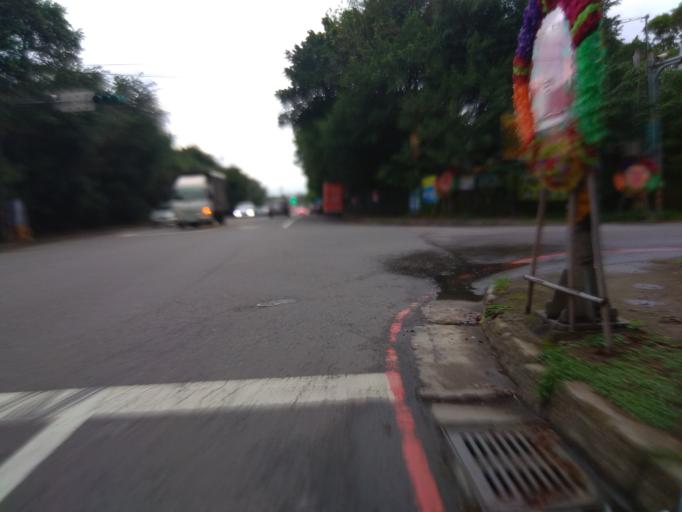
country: TW
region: Taiwan
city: Daxi
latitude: 24.9282
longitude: 121.1740
